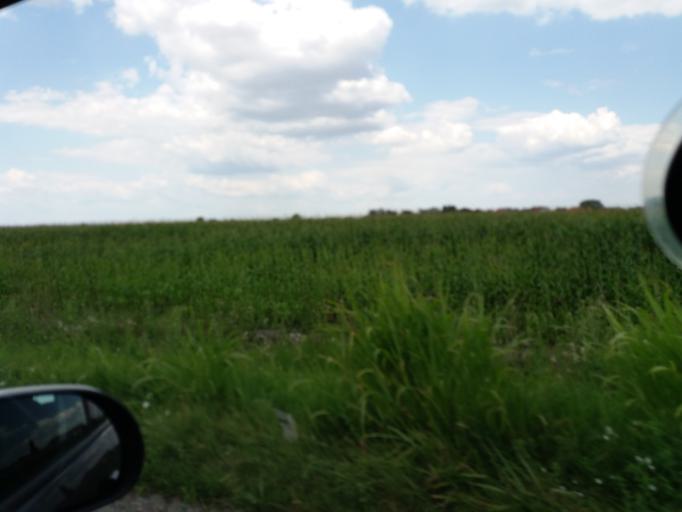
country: RS
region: Autonomna Pokrajina Vojvodina
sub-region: Sremski Okrug
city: Pecinci
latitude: 44.8974
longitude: 19.9642
